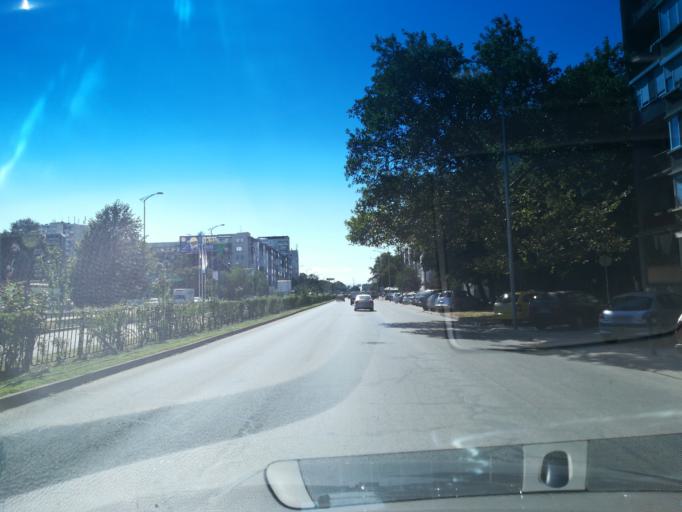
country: BG
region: Plovdiv
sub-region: Obshtina Plovdiv
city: Plovdiv
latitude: 42.1590
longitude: 24.7353
